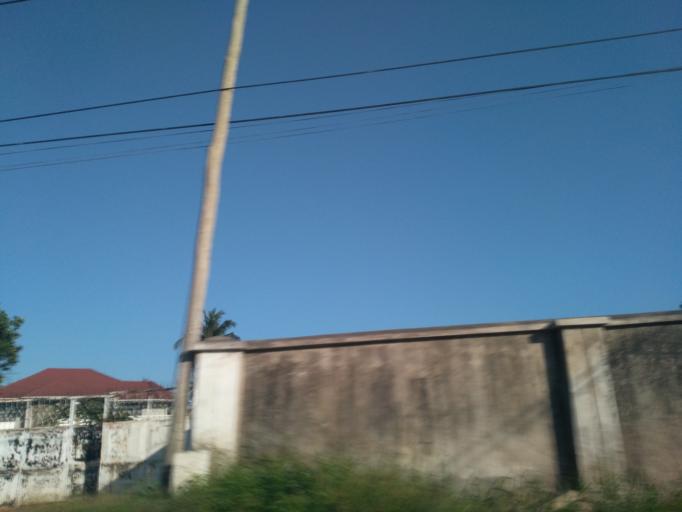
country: TZ
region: Dar es Salaam
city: Magomeni
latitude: -6.7509
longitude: 39.2390
